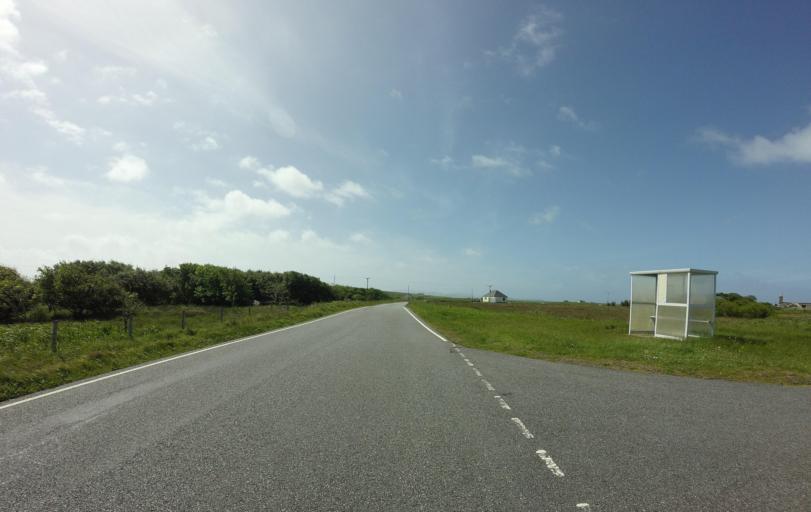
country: GB
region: Scotland
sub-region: Eilean Siar
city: Isle of South Uist
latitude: 57.1163
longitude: -7.3646
